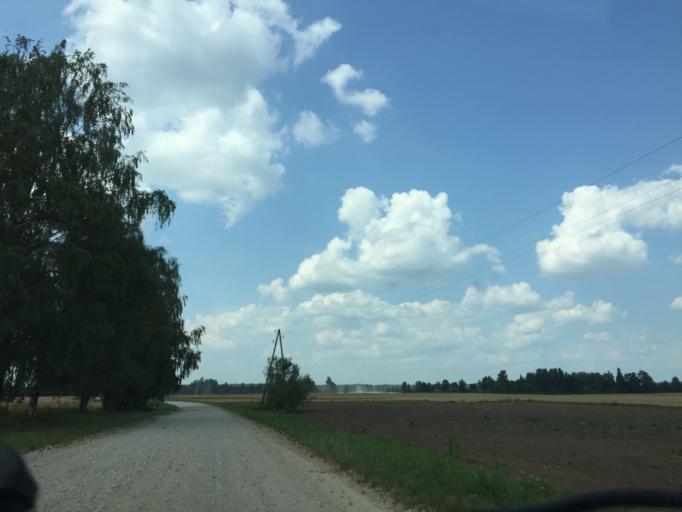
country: LT
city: Zagare
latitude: 56.3432
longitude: 23.1473
